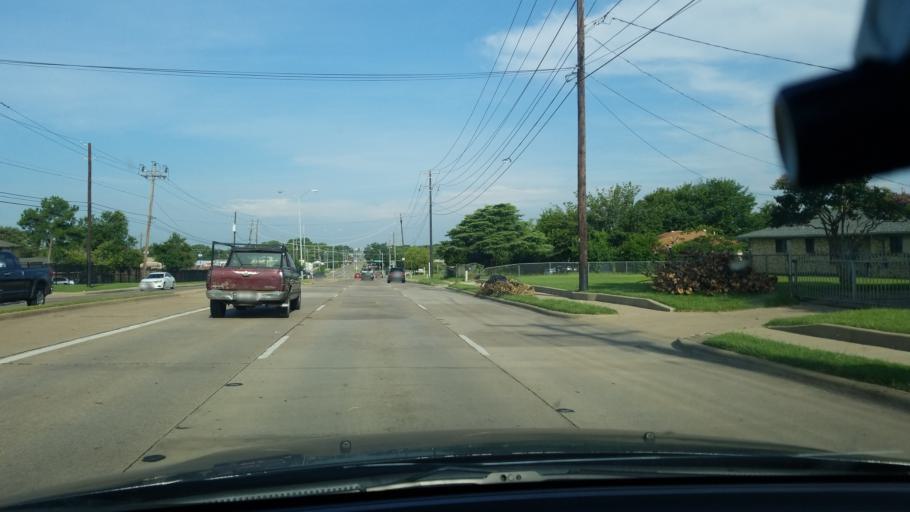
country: US
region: Texas
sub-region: Dallas County
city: Balch Springs
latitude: 32.7342
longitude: -96.6537
